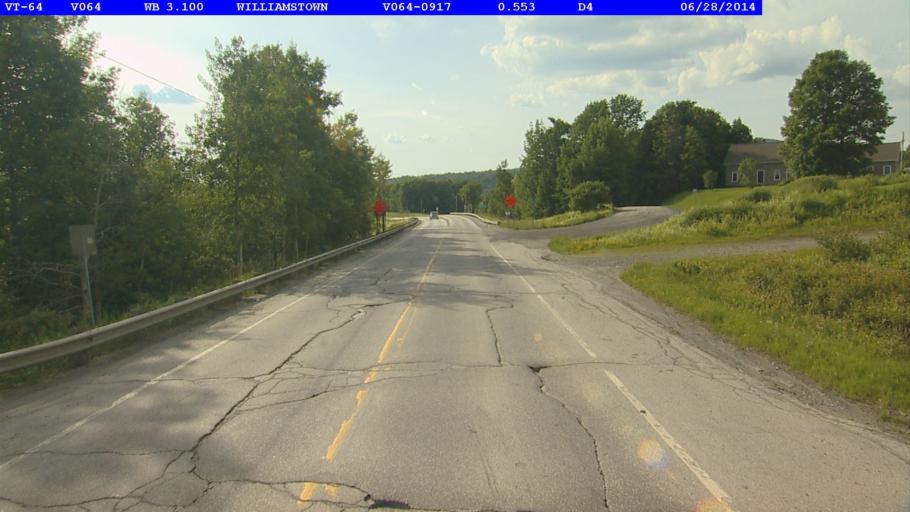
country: US
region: Vermont
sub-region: Orange County
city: Williamstown
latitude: 44.1132
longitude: -72.6030
